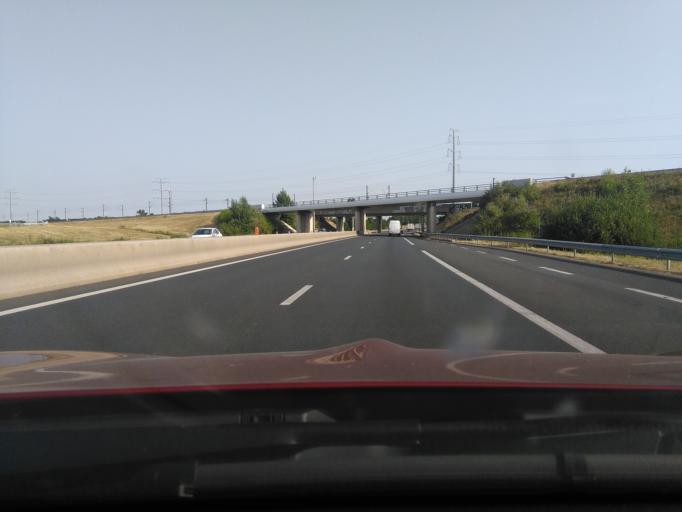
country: FR
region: Rhone-Alpes
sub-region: Departement du Rhone
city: Cailloux-sur-Fontaines
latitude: 45.8620
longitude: 4.9074
